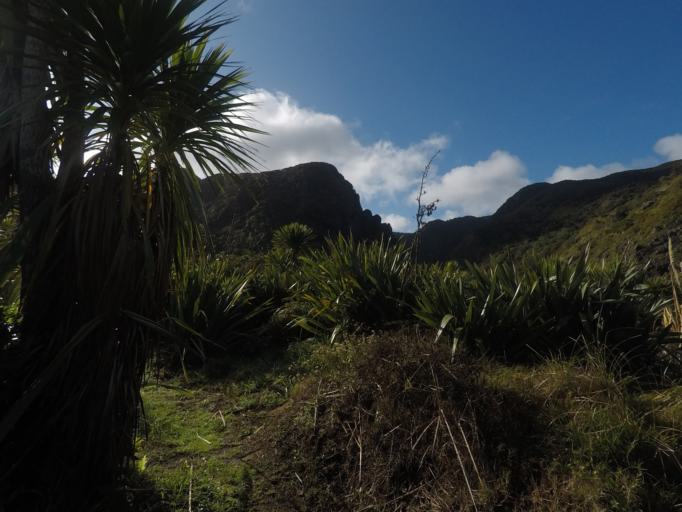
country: NZ
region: Auckland
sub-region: Auckland
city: Titirangi
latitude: -37.0102
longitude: 174.4871
